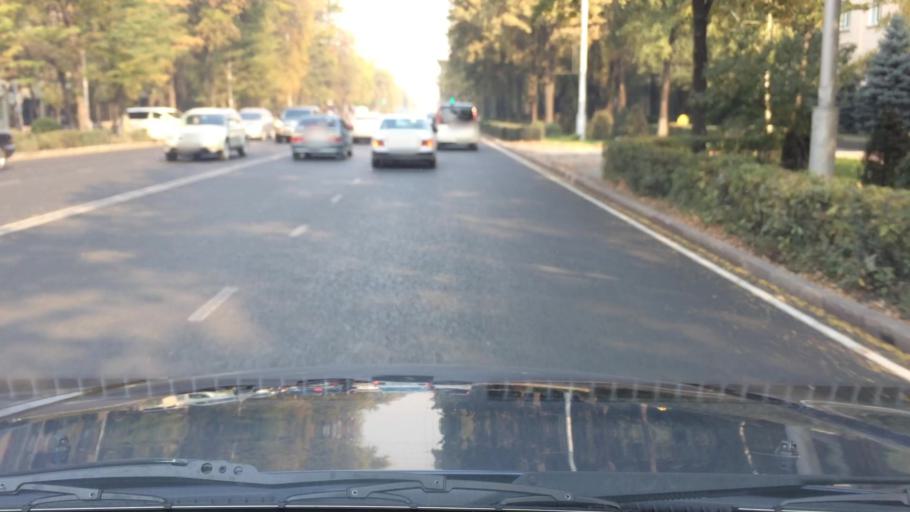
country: KG
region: Chuy
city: Bishkek
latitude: 42.8518
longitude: 74.5865
